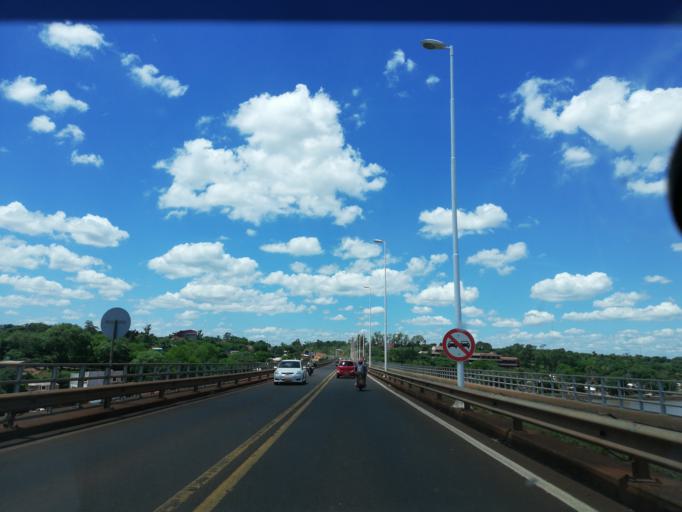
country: AR
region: Misiones
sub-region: Departamento de Capital
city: Posadas
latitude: -27.3682
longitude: -55.8594
